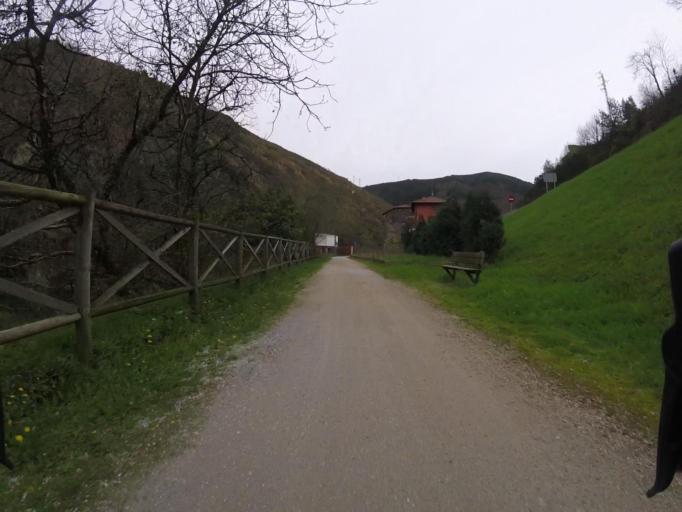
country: ES
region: Navarre
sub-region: Provincia de Navarra
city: Bera
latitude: 43.2954
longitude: -1.7302
